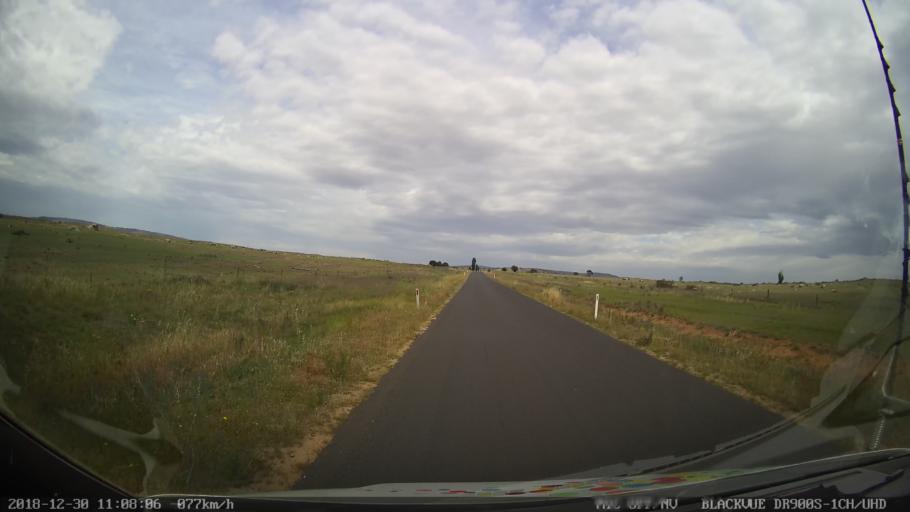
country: AU
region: New South Wales
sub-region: Snowy River
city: Berridale
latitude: -36.5021
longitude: 148.8113
